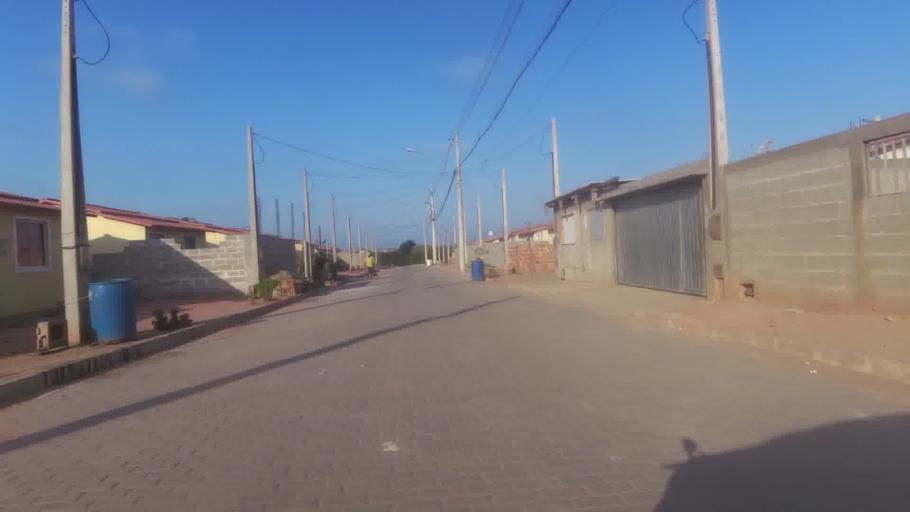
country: BR
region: Espirito Santo
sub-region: Itapemirim
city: Itapemirim
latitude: -21.0186
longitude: -40.8310
